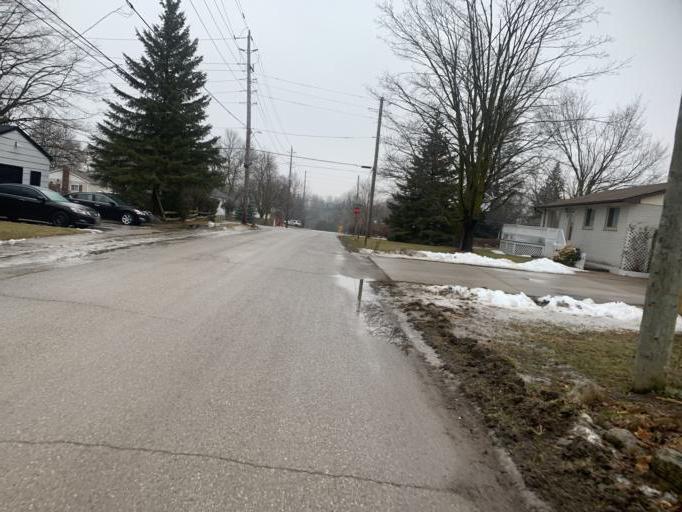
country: CA
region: Ontario
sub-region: Halton
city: Milton
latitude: 43.6574
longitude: -79.9220
